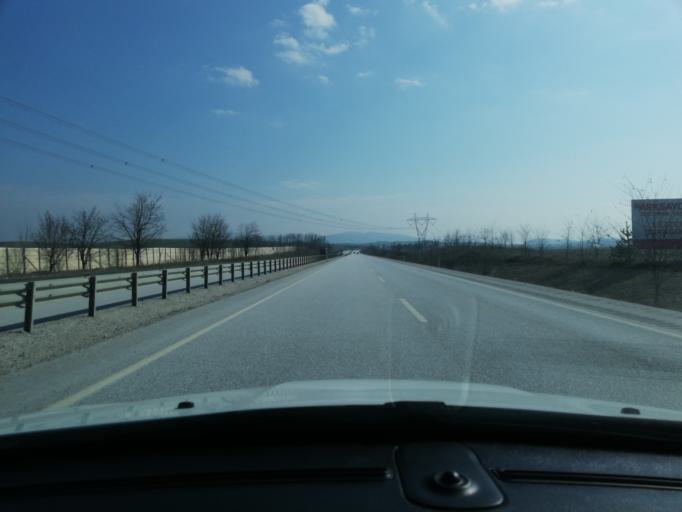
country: TR
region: Cankiri
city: Atkaracalar
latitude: 40.8372
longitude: 33.1544
